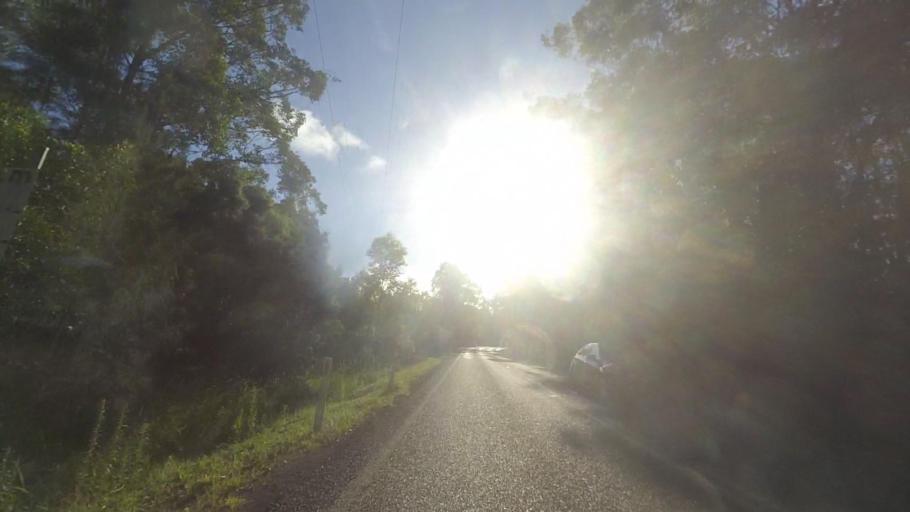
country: AU
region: New South Wales
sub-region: Great Lakes
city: Nabiac
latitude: -32.0912
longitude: 152.4426
